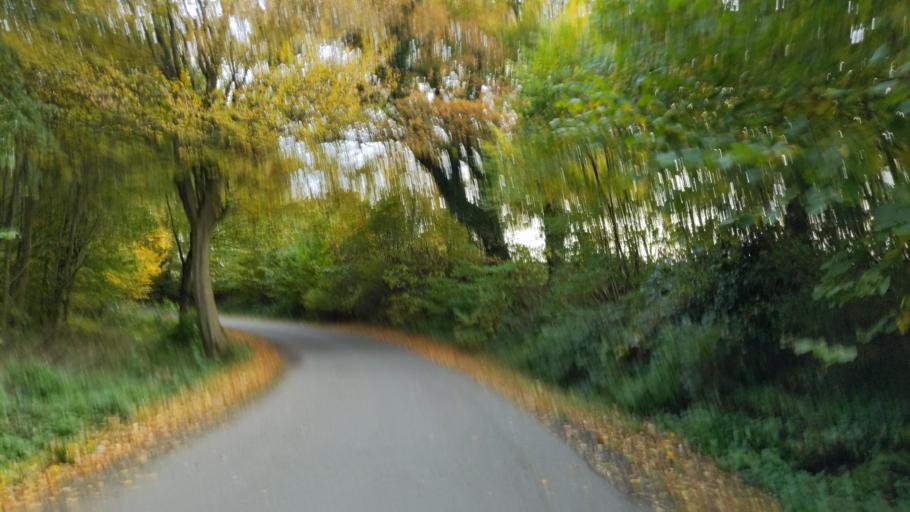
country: DE
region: Schleswig-Holstein
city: Kasseedorf
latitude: 54.1418
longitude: 10.6986
